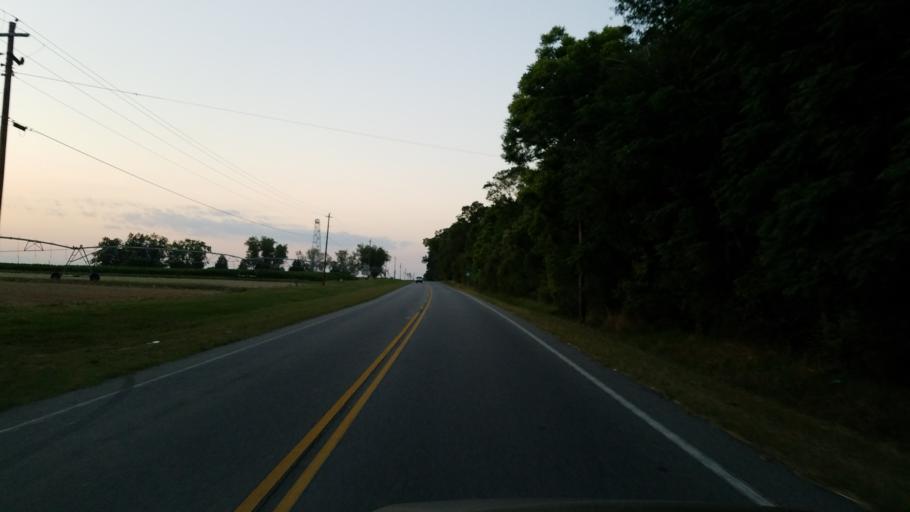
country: US
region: Georgia
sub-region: Tift County
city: Tifton
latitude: 31.4857
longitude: -83.5189
